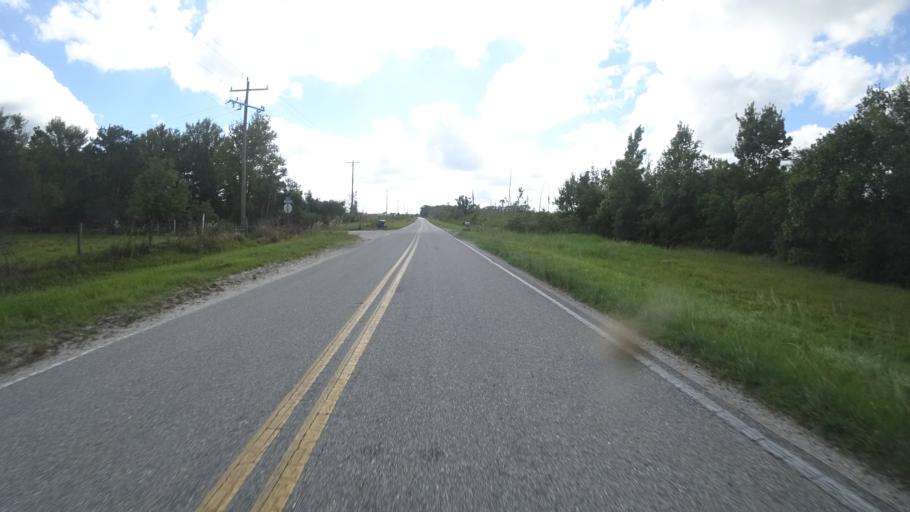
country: US
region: Florida
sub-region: Sarasota County
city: Lake Sarasota
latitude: 27.4077
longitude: -82.1333
